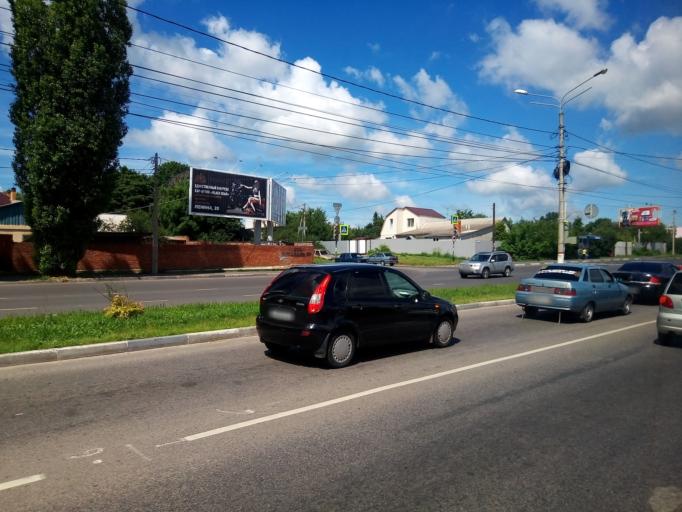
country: RU
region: Kursk
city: Kursk
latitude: 51.7314
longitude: 36.1559
